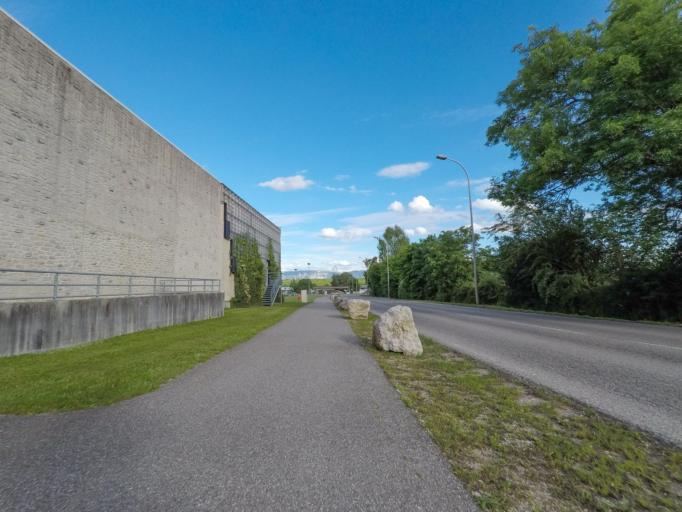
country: FR
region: Rhone-Alpes
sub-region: Departement de l'Ain
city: Thoiry
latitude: 46.2283
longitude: 5.9903
